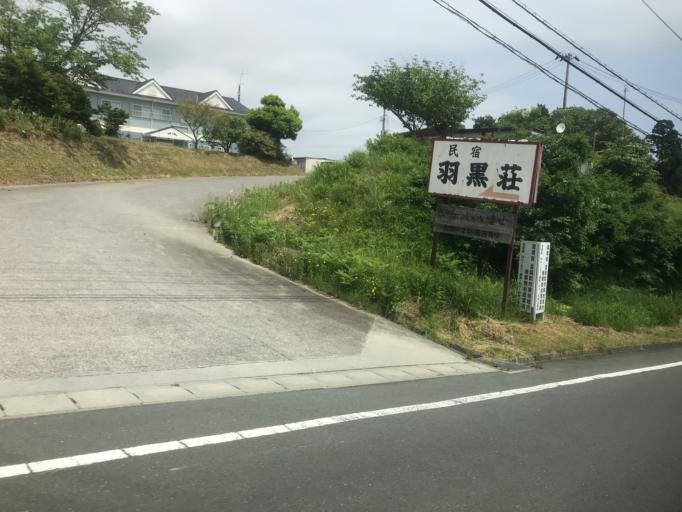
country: JP
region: Fukushima
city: Iwaki
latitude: 37.2500
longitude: 140.9963
